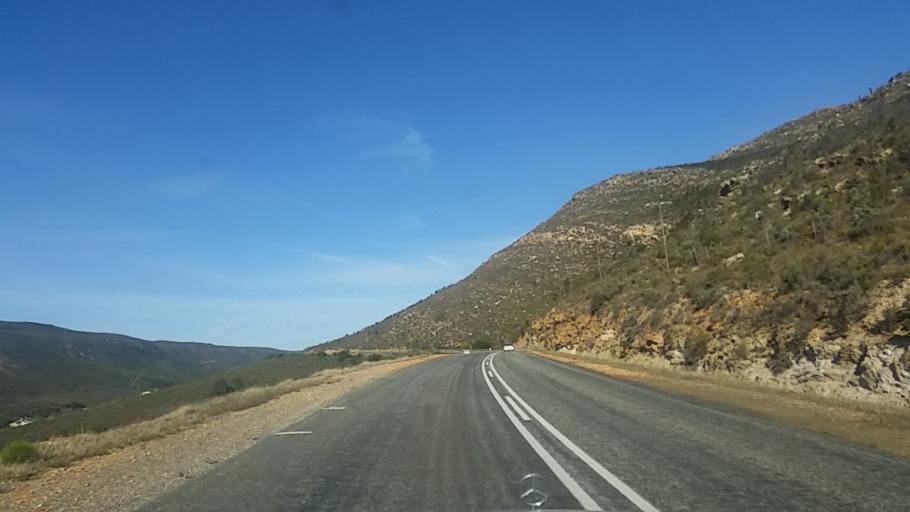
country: ZA
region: Western Cape
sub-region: Eden District Municipality
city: Knysna
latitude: -33.7482
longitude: 22.9764
